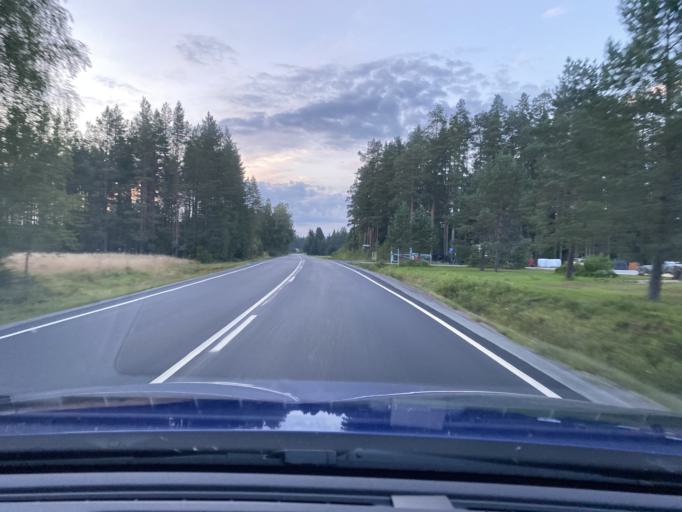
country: FI
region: Satakunta
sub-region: Pohjois-Satakunta
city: Honkajoki
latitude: 62.0704
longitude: 22.2499
